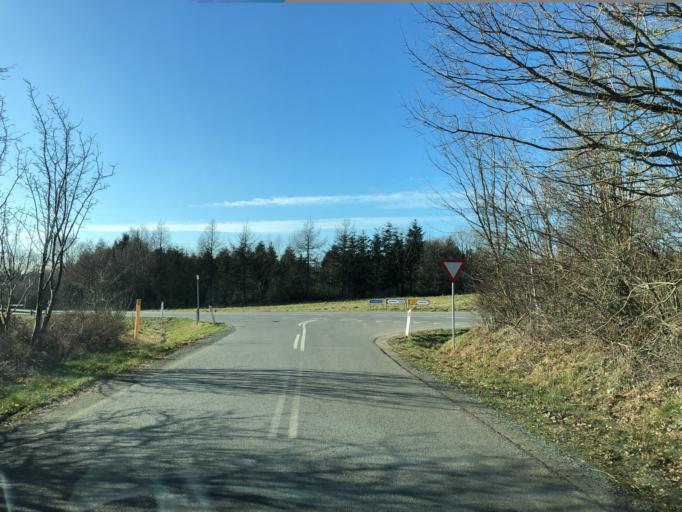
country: DK
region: Central Jutland
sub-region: Ikast-Brande Kommune
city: Bording Kirkeby
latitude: 56.1559
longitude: 9.2341
